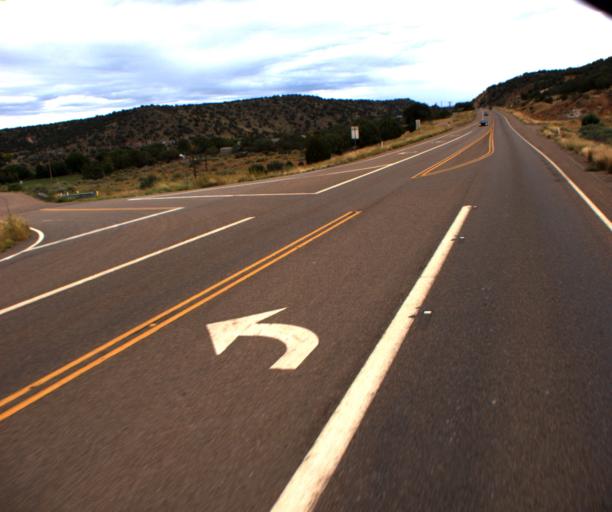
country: US
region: Arizona
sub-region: Navajo County
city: Taylor
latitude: 34.4064
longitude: -110.0771
